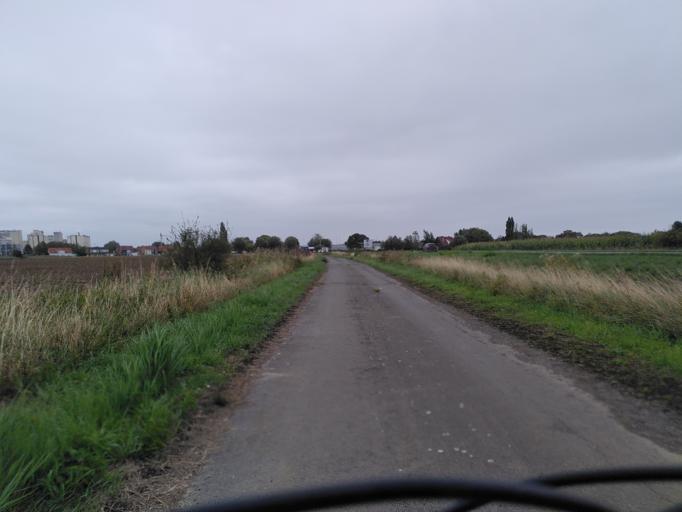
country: FR
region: Nord-Pas-de-Calais
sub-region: Departement du Pas-de-Calais
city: Lestrem
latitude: 50.6301
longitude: 2.6733
